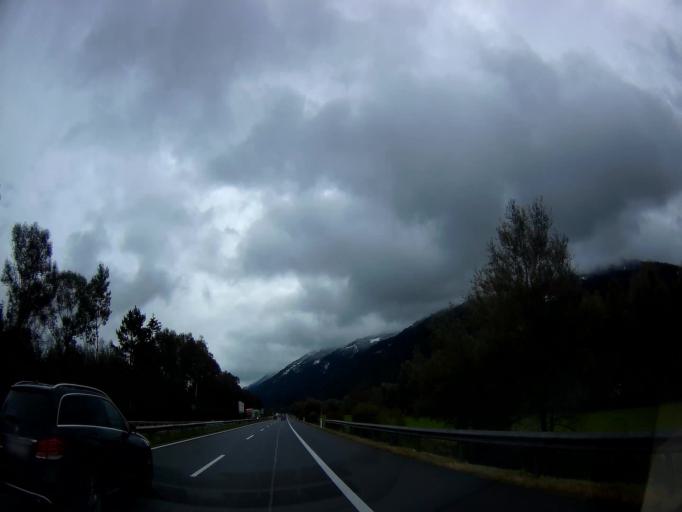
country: AT
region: Styria
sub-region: Politischer Bezirk Liezen
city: Trieben
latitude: 47.4957
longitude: 14.4939
